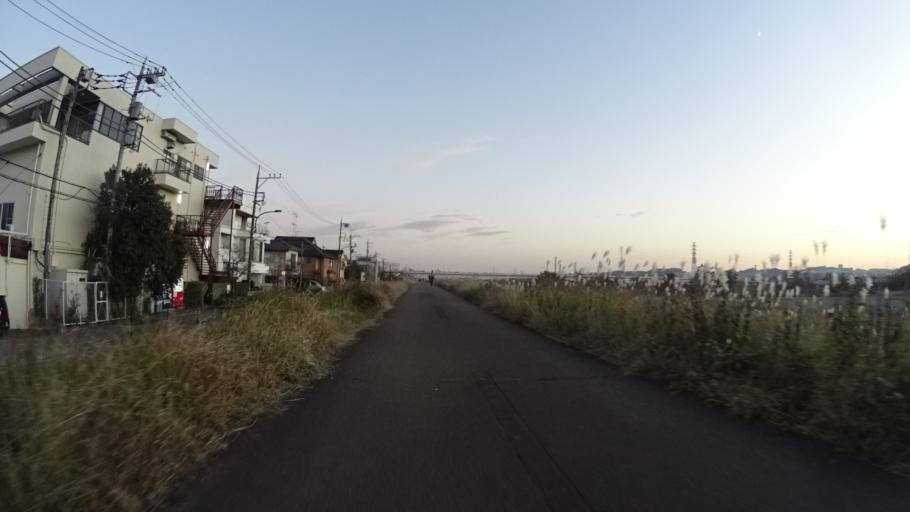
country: JP
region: Tokyo
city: Hino
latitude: 35.6781
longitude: 139.4248
